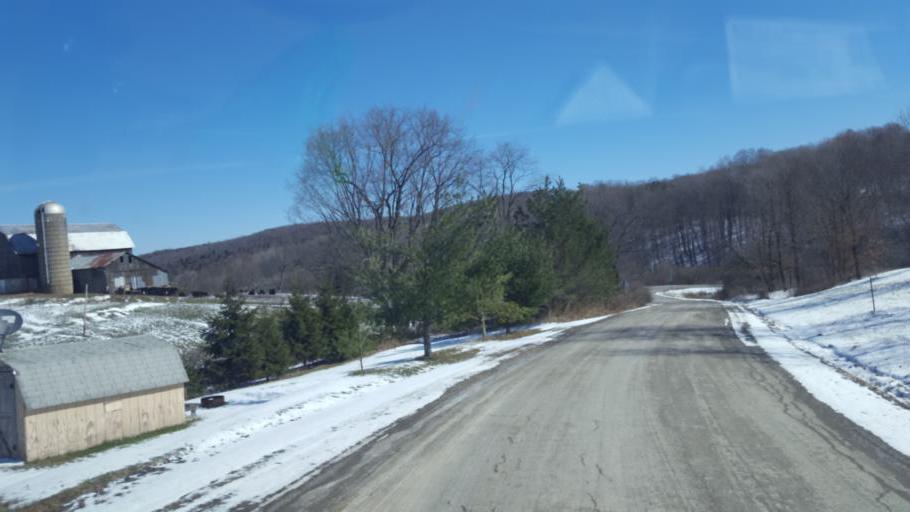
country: US
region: New York
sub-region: Allegany County
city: Andover
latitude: 42.0088
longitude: -77.7634
